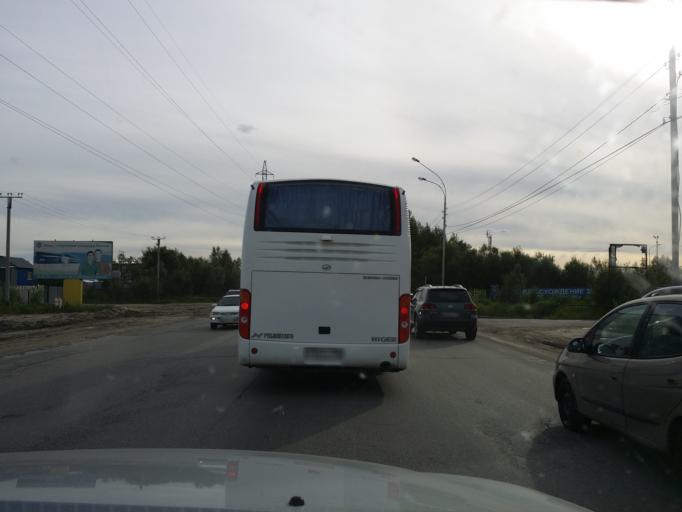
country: RU
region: Khanty-Mansiyskiy Avtonomnyy Okrug
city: Nizhnevartovsk
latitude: 60.9444
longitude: 76.6433
